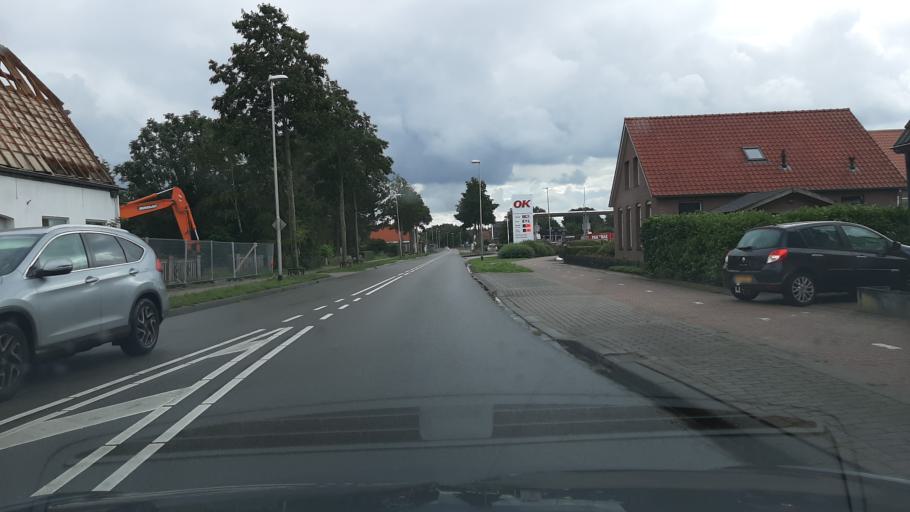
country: NL
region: Overijssel
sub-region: Gemeente Steenwijkerland
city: Steenwijkerwold
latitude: 52.8084
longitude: 6.0789
